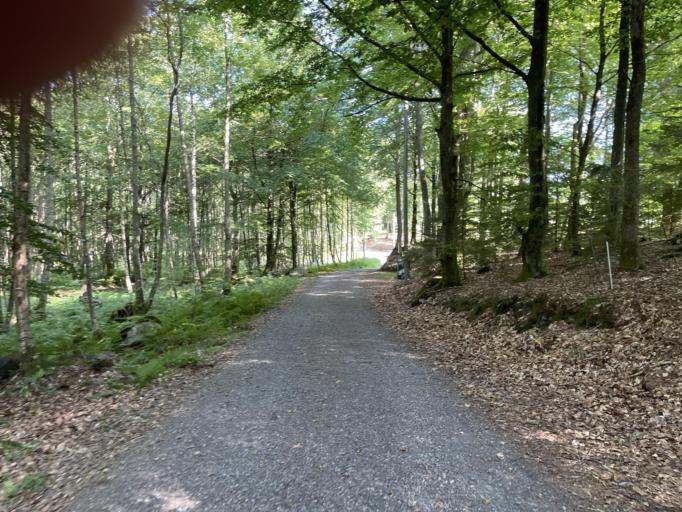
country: SE
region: Skane
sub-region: Hoors Kommun
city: Hoeoer
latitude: 55.9898
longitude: 13.5831
